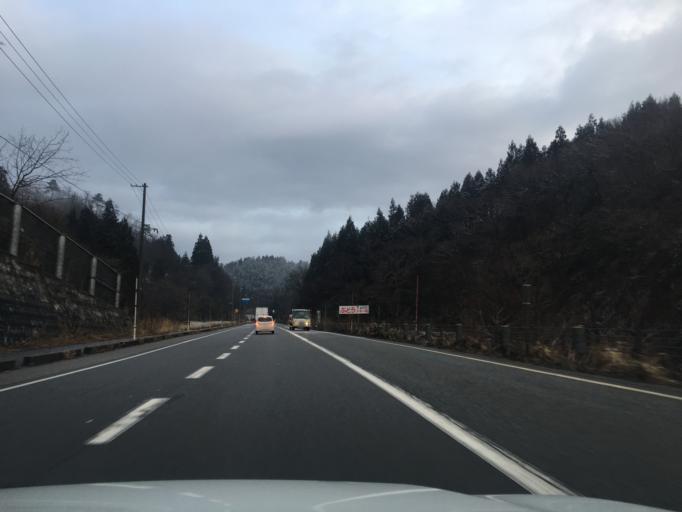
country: JP
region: Niigata
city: Murakami
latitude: 38.3767
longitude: 139.5566
